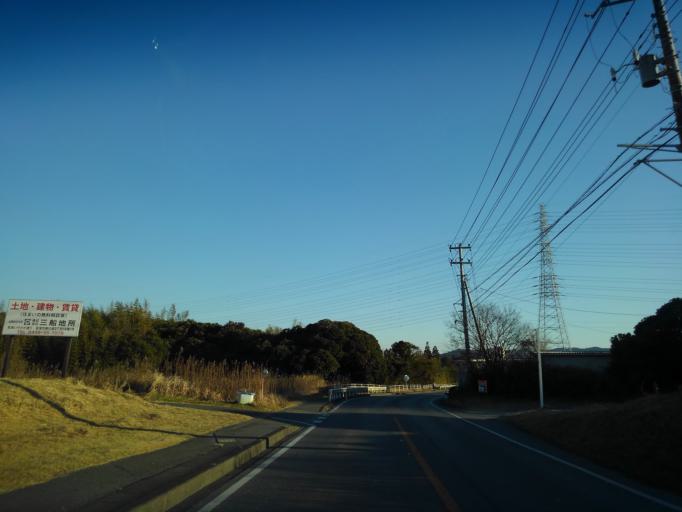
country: JP
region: Chiba
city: Kimitsu
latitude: 35.3124
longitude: 139.9361
